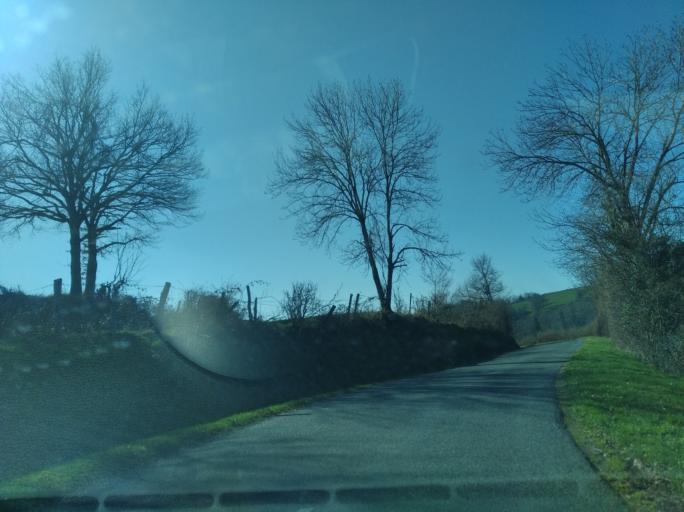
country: FR
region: Auvergne
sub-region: Departement de l'Allier
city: Le Mayet-de-Montagne
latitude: 46.0981
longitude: 3.6797
